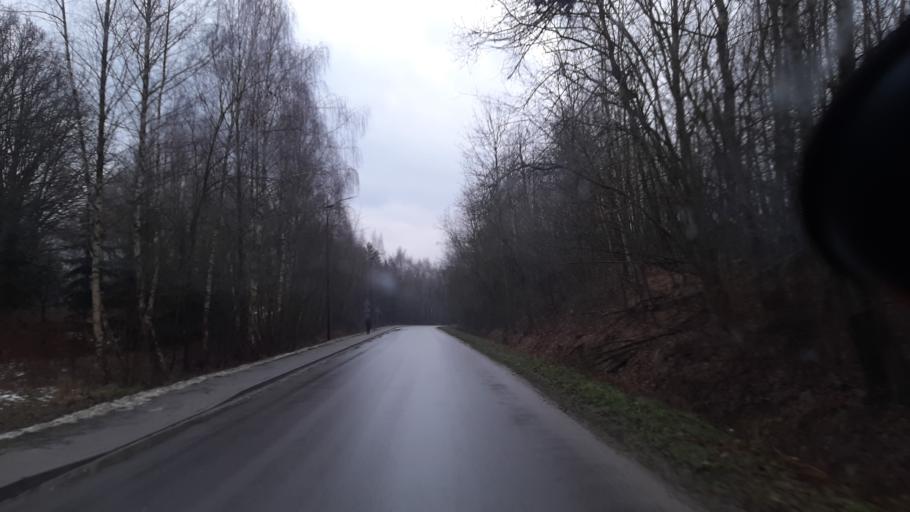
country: PL
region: Lublin Voivodeship
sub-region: Powiat lubelski
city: Lublin
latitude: 51.3201
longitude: 22.5612
